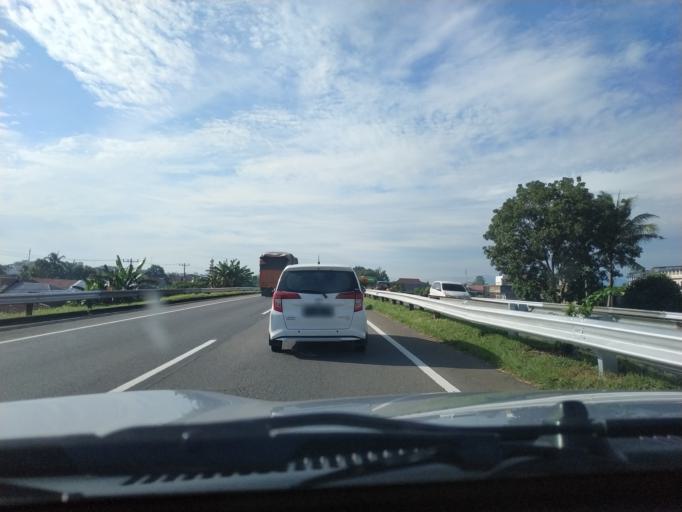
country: ID
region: North Sumatra
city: Medan
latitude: 3.5731
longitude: 98.7254
